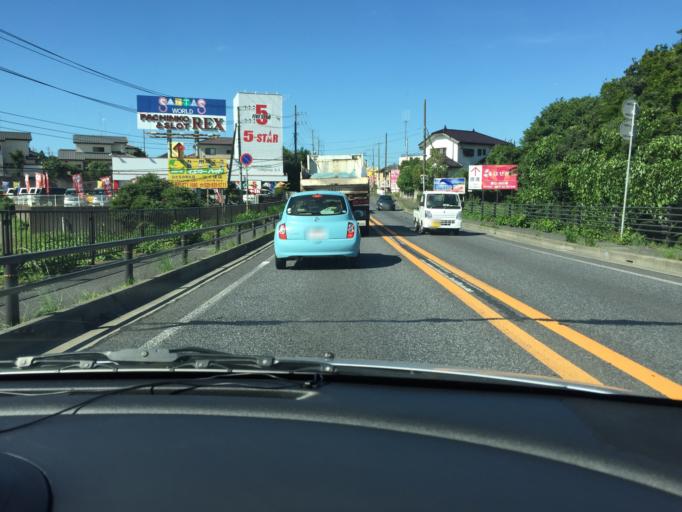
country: JP
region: Ibaraki
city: Naka
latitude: 36.0517
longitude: 140.1724
